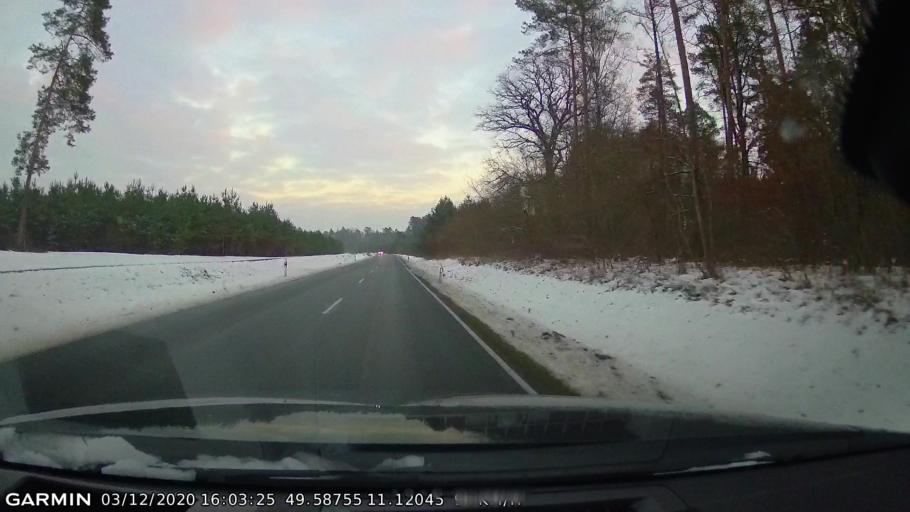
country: DE
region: Bavaria
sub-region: Upper Franconia
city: Dormitz
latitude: 49.5875
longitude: 11.1207
